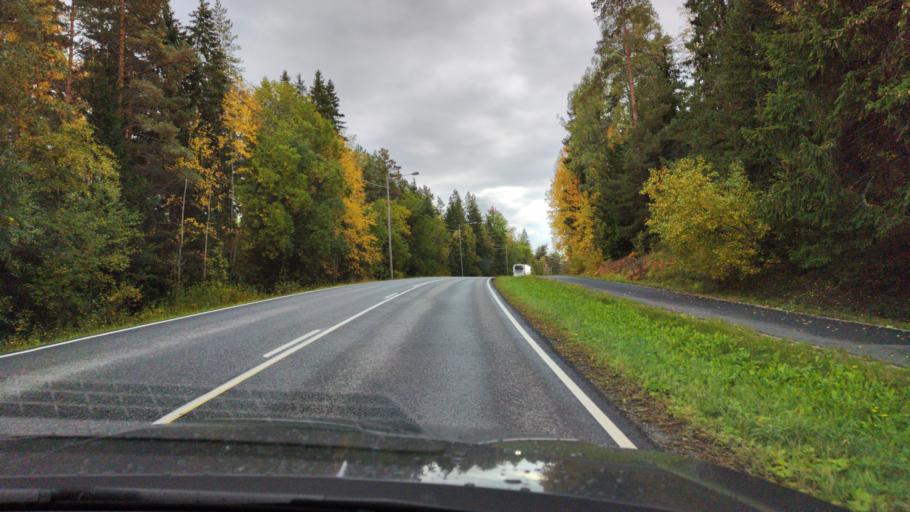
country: FI
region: Varsinais-Suomi
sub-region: Turku
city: Raisio
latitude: 60.3631
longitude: 22.1786
